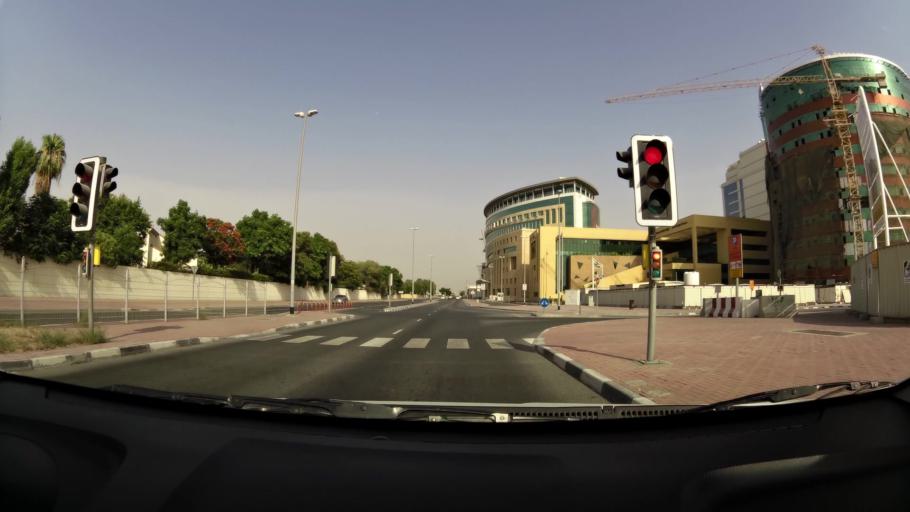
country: AE
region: Ash Shariqah
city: Sharjah
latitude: 25.2357
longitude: 55.3540
